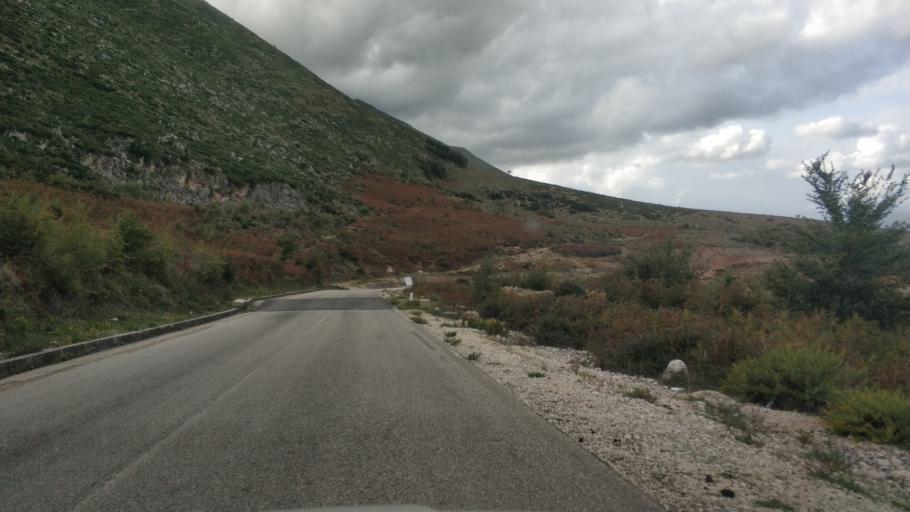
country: AL
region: Vlore
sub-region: Rrethi i Vlores
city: Orikum
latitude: 40.2635
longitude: 19.5189
